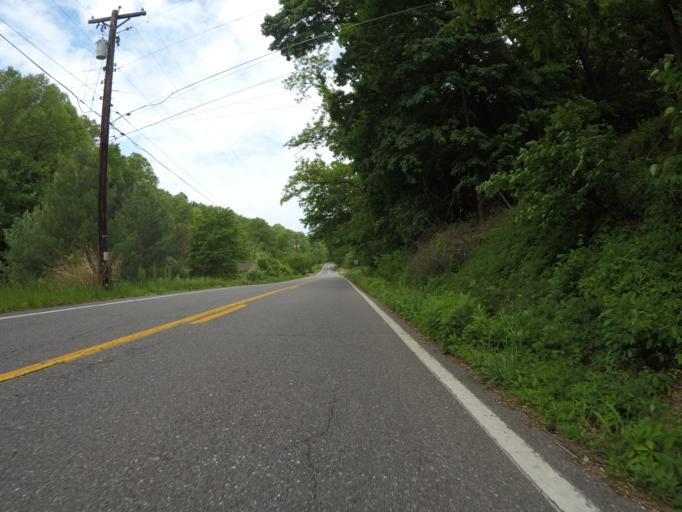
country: US
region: West Virginia
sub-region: Wayne County
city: Ceredo
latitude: 38.3548
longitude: -82.5518
